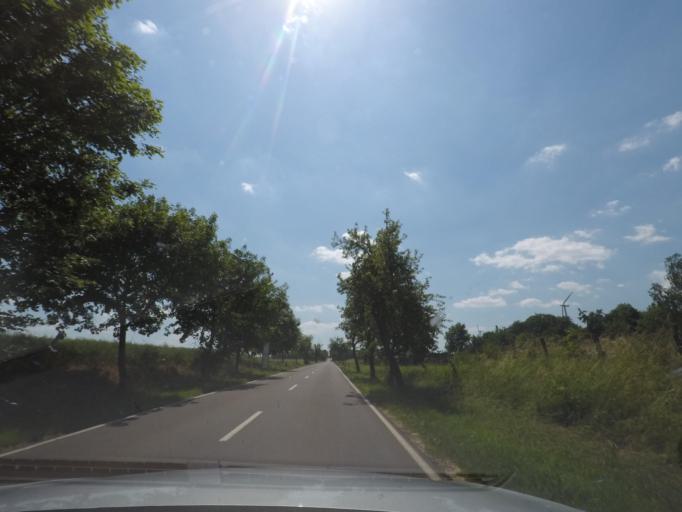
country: DE
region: Saxony-Anhalt
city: Eichenbarleben
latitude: 52.2104
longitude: 11.3949
